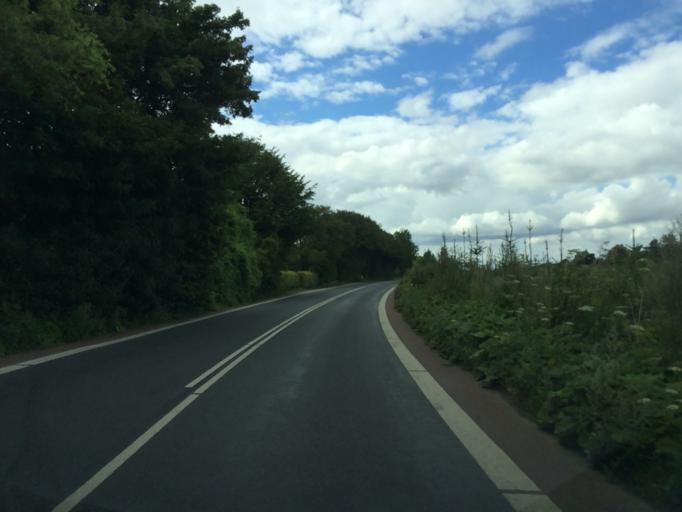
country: DK
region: South Denmark
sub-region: Assens Kommune
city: Harby
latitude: 55.1576
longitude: 10.1428
